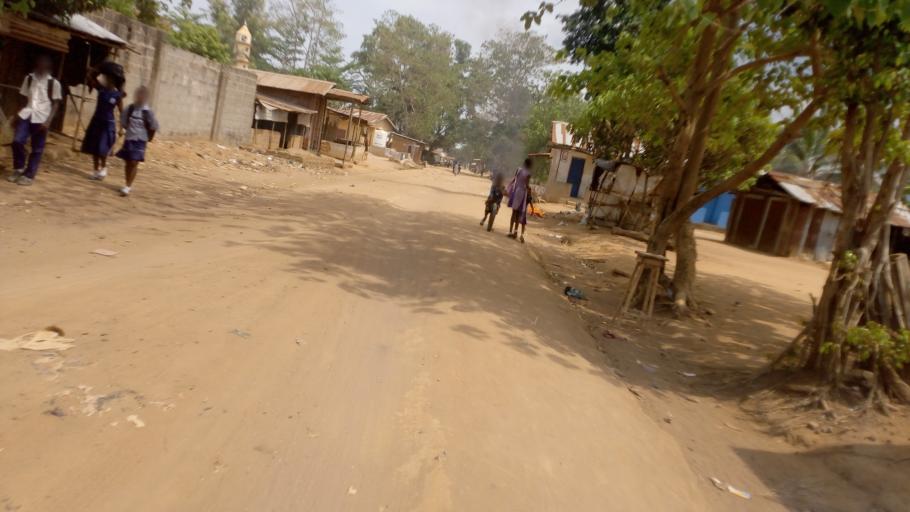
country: SL
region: Western Area
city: Waterloo
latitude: 8.3172
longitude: -13.0651
